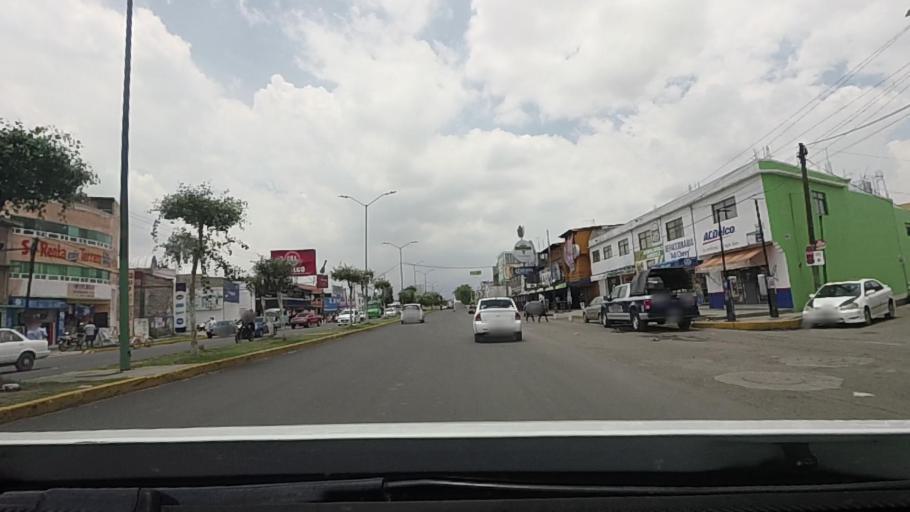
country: MX
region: Mexico
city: Chalco de Diaz Covarrubias
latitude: 19.2666
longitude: -98.8965
